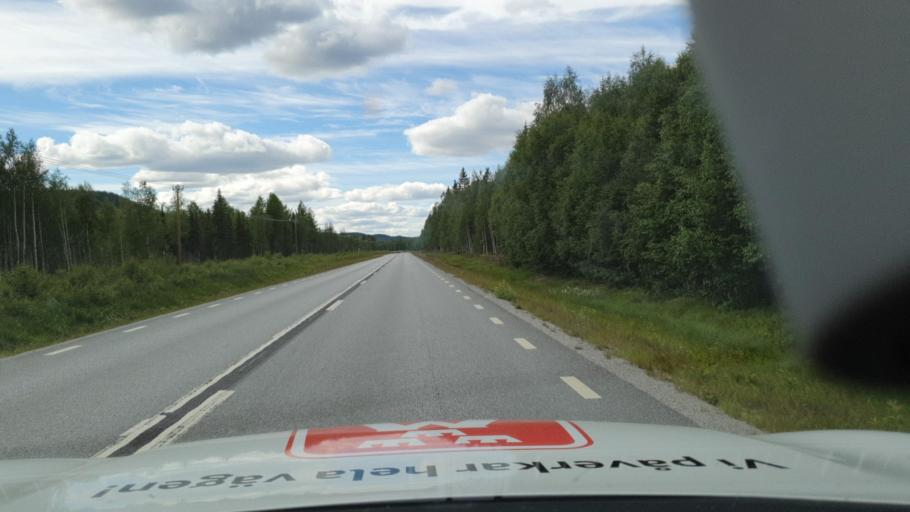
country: SE
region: Vaesterbotten
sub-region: Asele Kommun
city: Insjon
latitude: 64.1582
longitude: 17.8380
